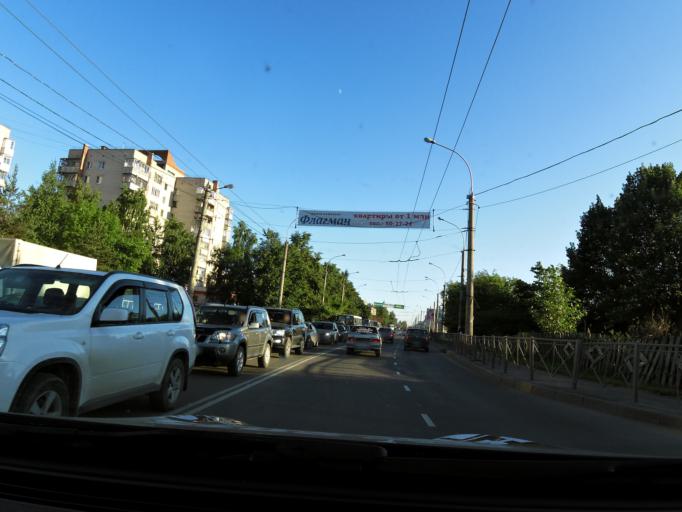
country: RU
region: Vologda
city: Vologda
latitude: 59.1984
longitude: 39.9105
